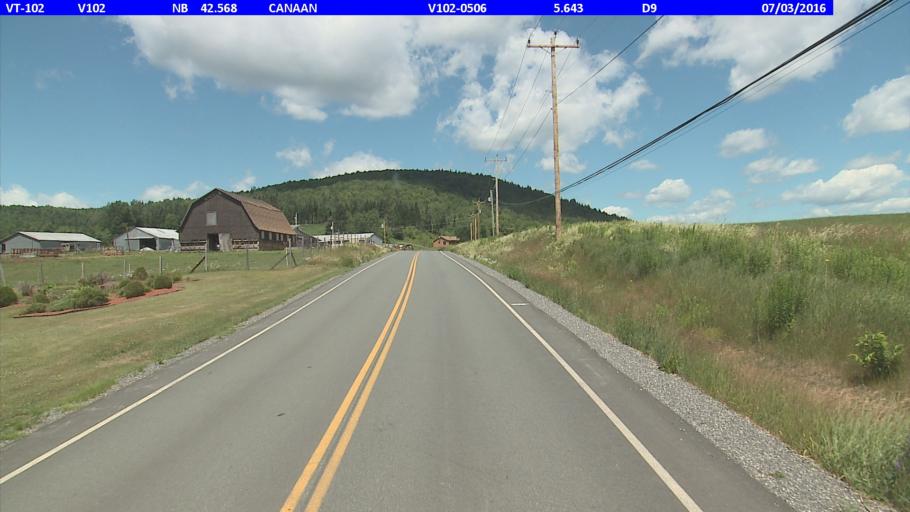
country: US
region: New Hampshire
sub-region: Coos County
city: Colebrook
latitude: 44.9802
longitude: -71.5422
